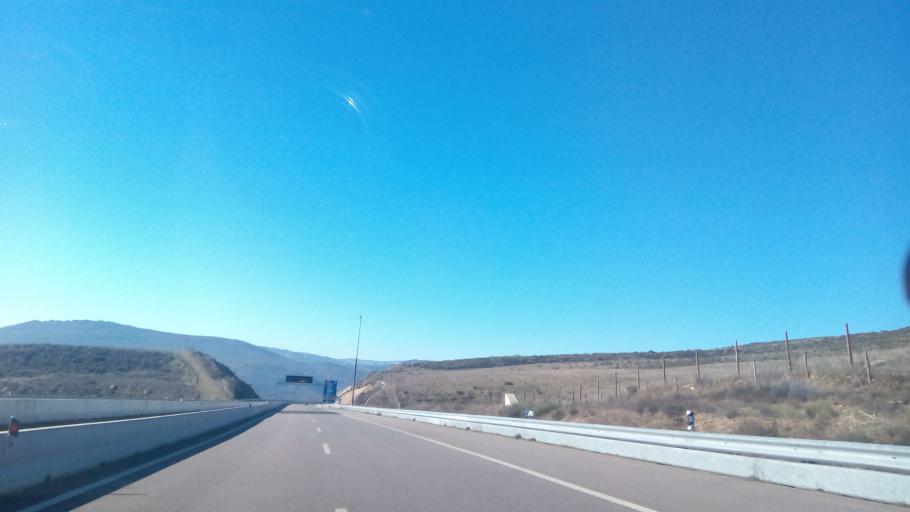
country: PT
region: Braganca
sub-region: Braganca Municipality
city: Braganca
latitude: 41.7814
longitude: -6.6947
